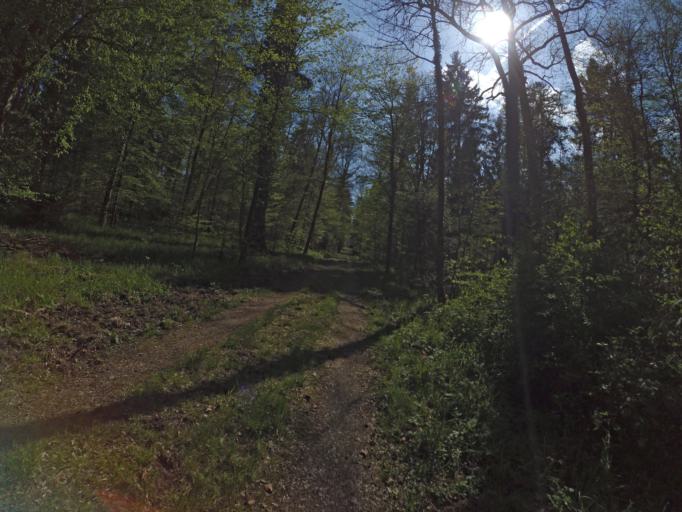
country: CH
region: Thurgau
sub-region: Frauenfeld District
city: Diessenhofen
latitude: 47.6517
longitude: 8.7466
